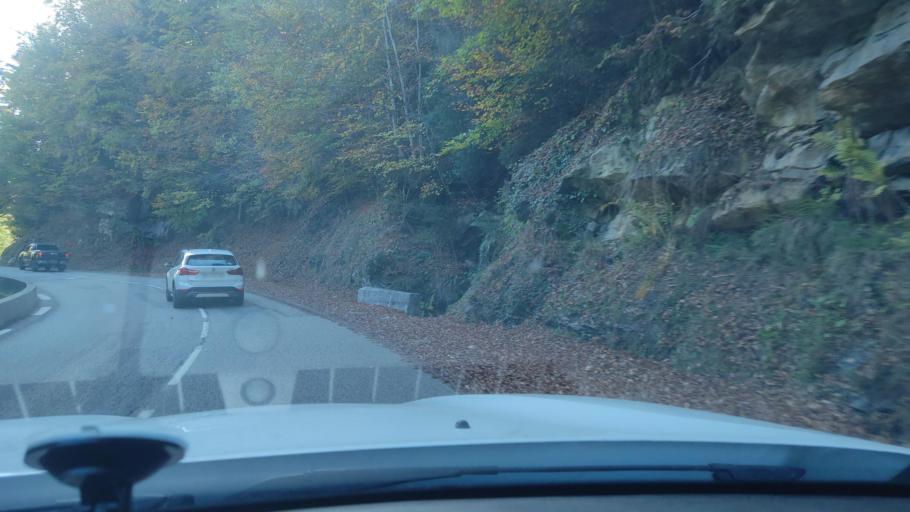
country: FR
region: Rhone-Alpes
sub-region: Departement de la Savoie
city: Ugine
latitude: 45.7822
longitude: 6.4812
